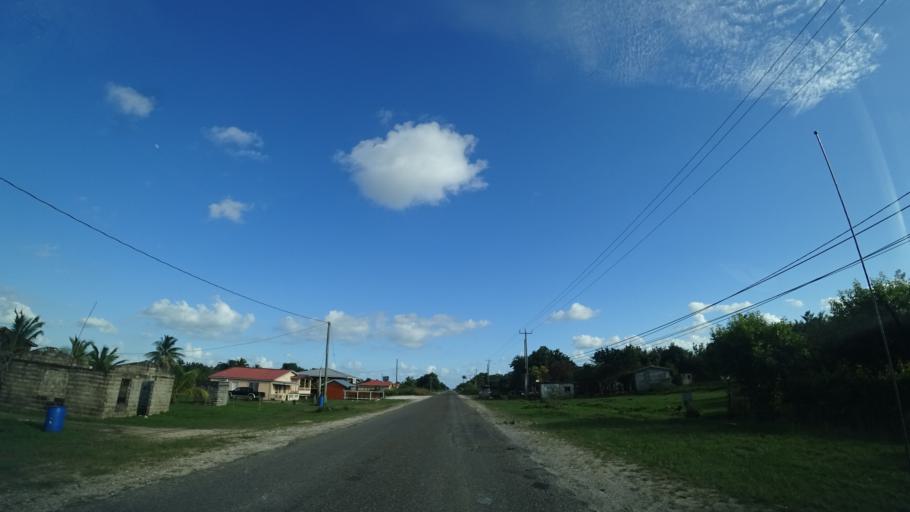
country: BZ
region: Belize
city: Belize City
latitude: 17.5787
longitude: -88.3426
